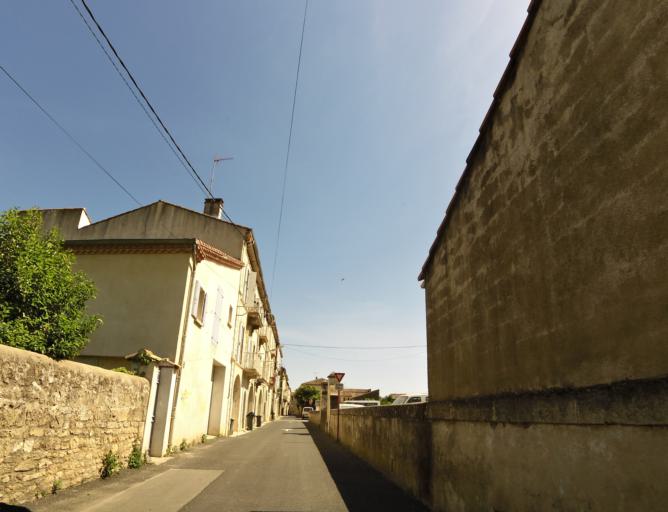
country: FR
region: Languedoc-Roussillon
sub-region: Departement du Gard
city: Sommieres
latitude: 43.7864
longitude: 4.0877
